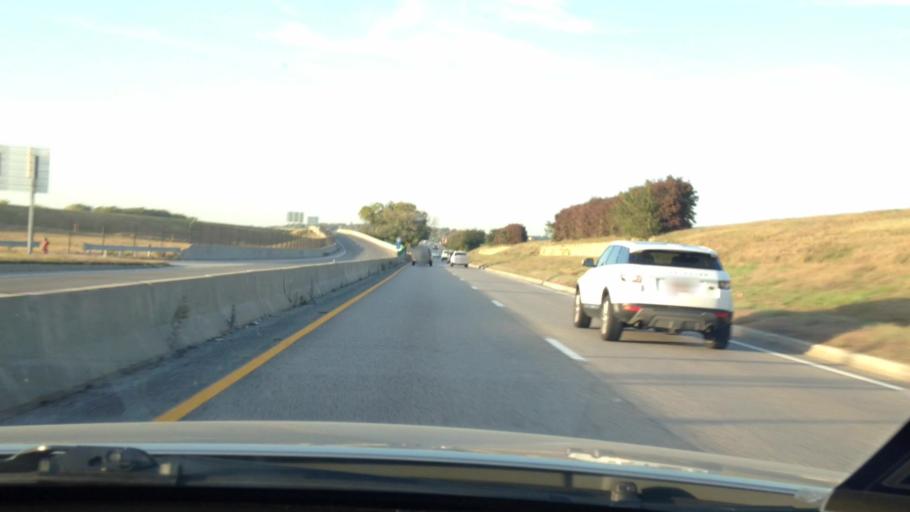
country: US
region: Missouri
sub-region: Clay County
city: North Kansas City
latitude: 39.1349
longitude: -94.5869
